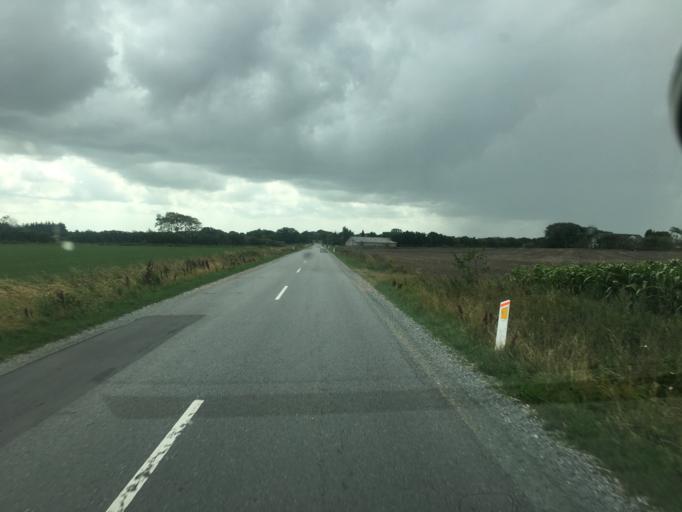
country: DK
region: South Denmark
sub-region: Tonder Kommune
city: Logumkloster
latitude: 55.0069
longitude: 8.9672
